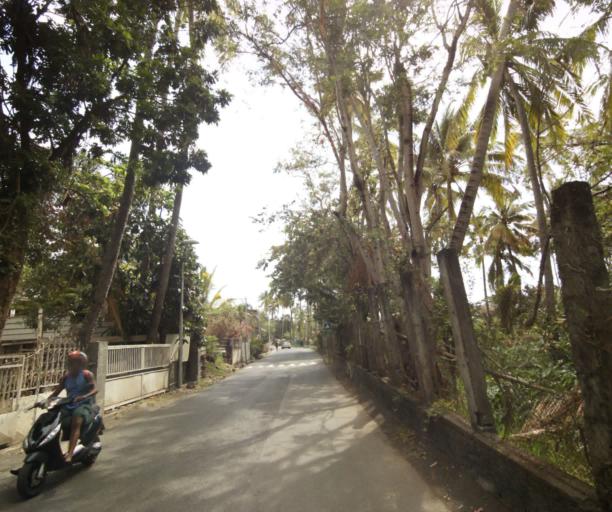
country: RE
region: Reunion
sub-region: Reunion
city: Saint-Paul
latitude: -21.0114
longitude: 55.2809
